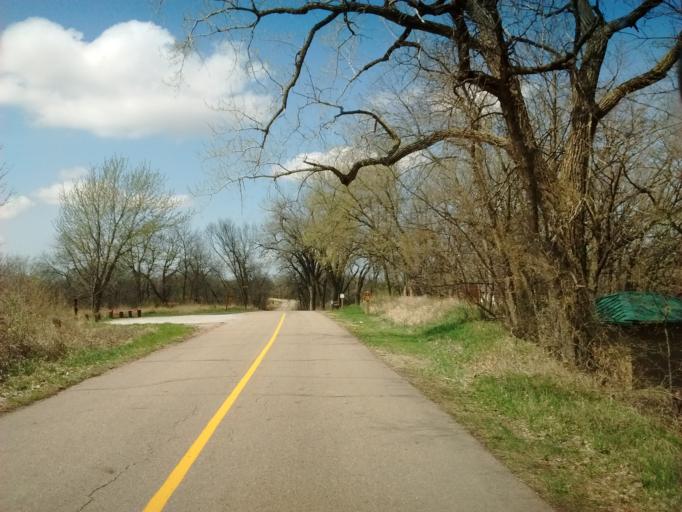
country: US
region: South Dakota
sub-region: Union County
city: North Sioux City
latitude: 42.5539
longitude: -96.4610
